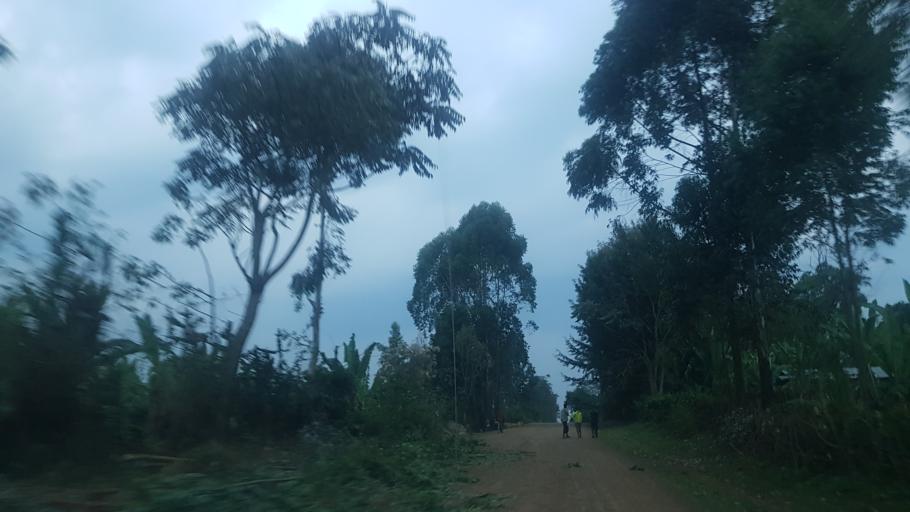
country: ET
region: Oromiya
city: Gore
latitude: 7.7656
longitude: 35.4724
